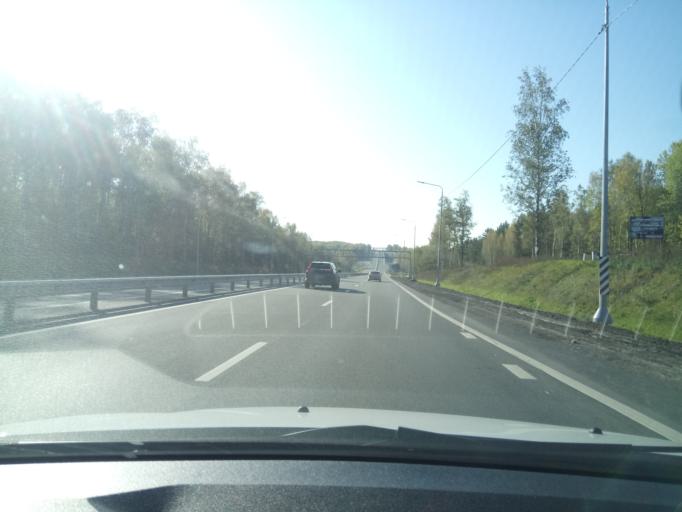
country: RU
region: Nizjnij Novgorod
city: Burevestnik
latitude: 56.0136
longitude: 43.9652
